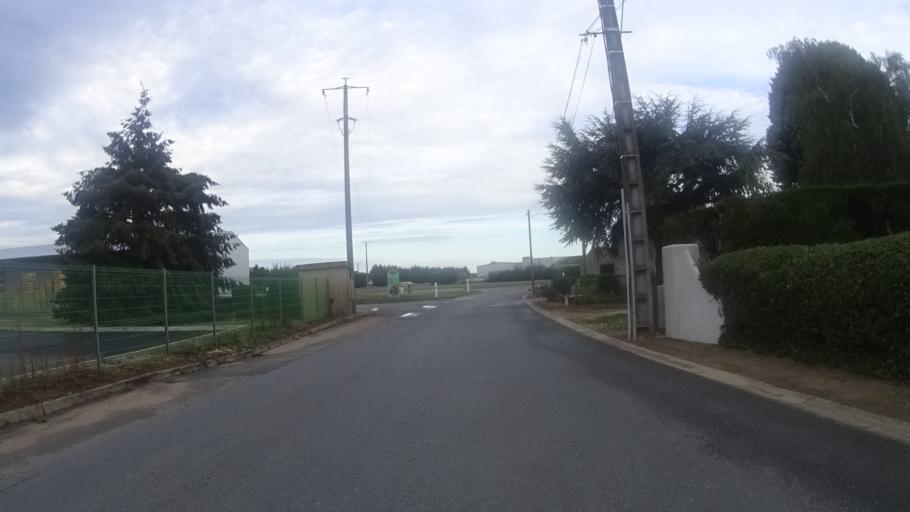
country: FR
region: Centre
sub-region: Departement du Loiret
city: Saint-Benoit-sur-Loire
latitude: 47.7920
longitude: 2.3143
